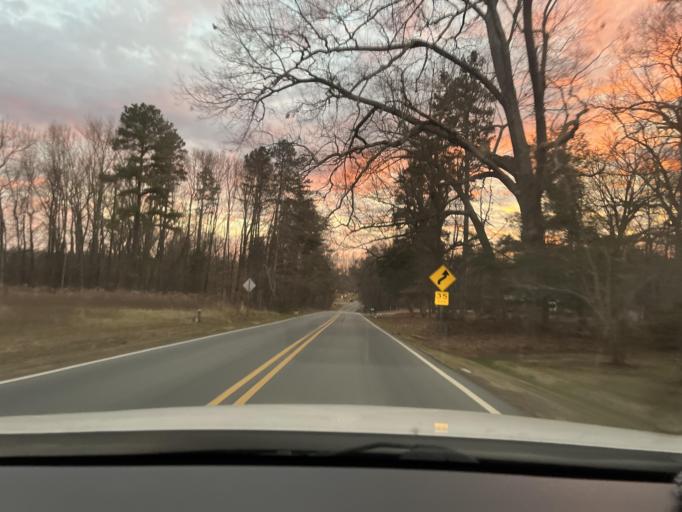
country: US
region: North Carolina
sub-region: Guilford County
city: Forest Oaks
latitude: 36.0142
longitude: -79.7287
